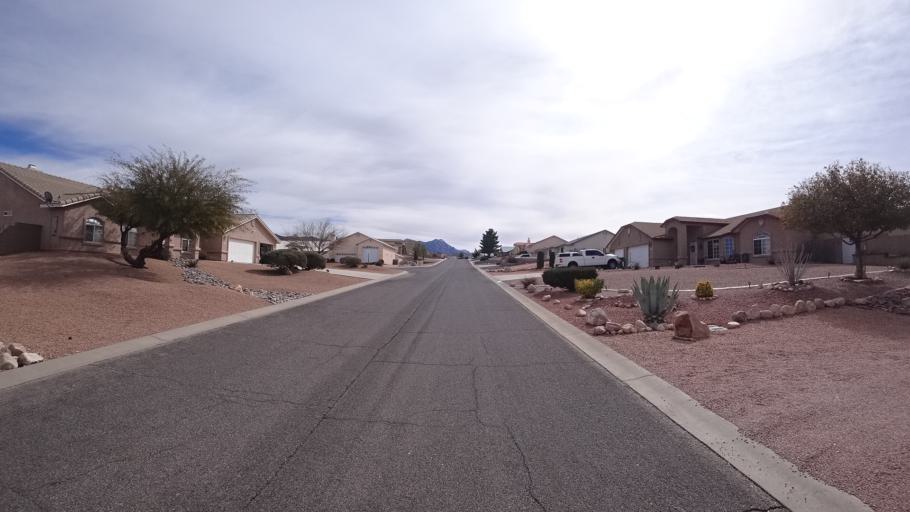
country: US
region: Arizona
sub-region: Mohave County
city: Kingman
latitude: 35.1923
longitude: -113.9807
